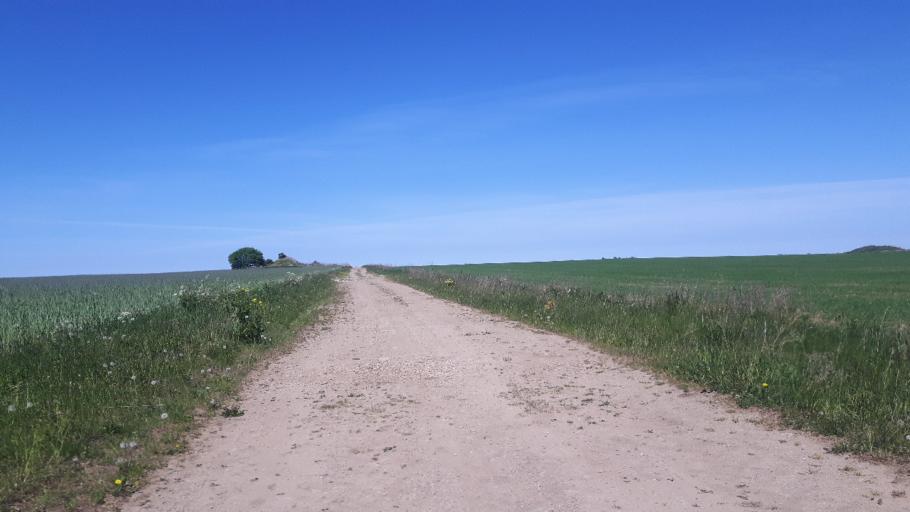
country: EE
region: Ida-Virumaa
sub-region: Toila vald
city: Voka
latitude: 59.4066
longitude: 27.6465
